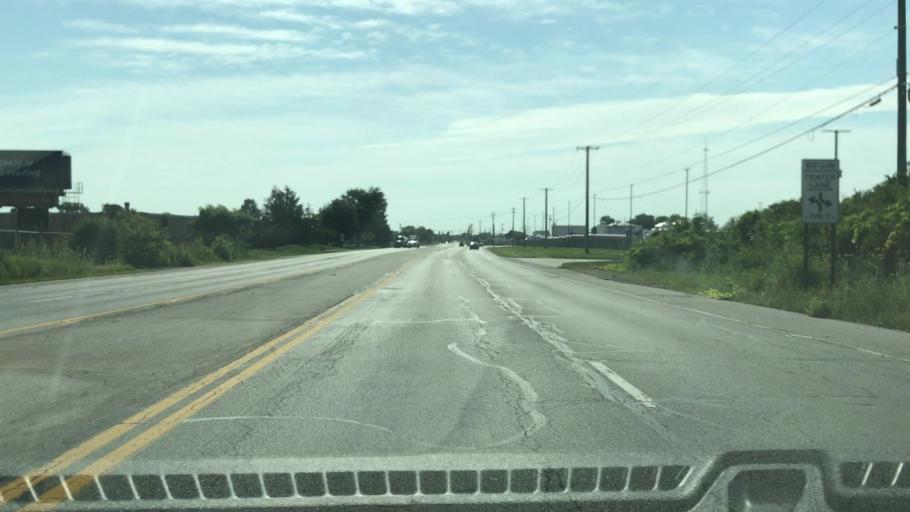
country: US
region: Ohio
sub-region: Franklin County
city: Lincoln Village
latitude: 39.9700
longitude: -83.1157
